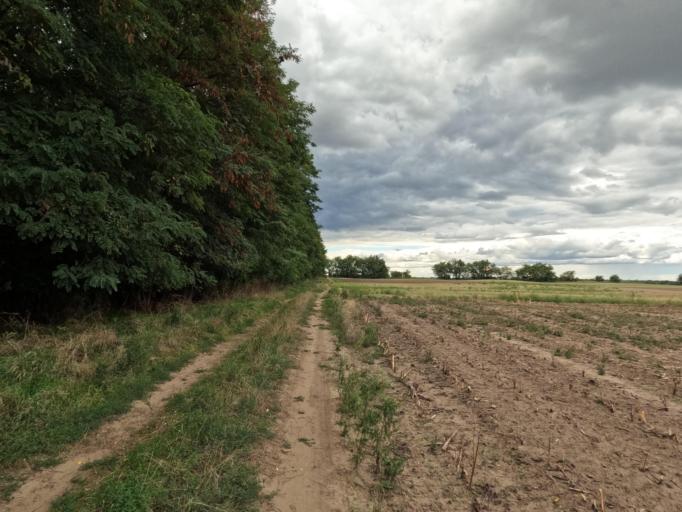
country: HU
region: Tolna
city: Tengelic
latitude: 46.5210
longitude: 18.6764
